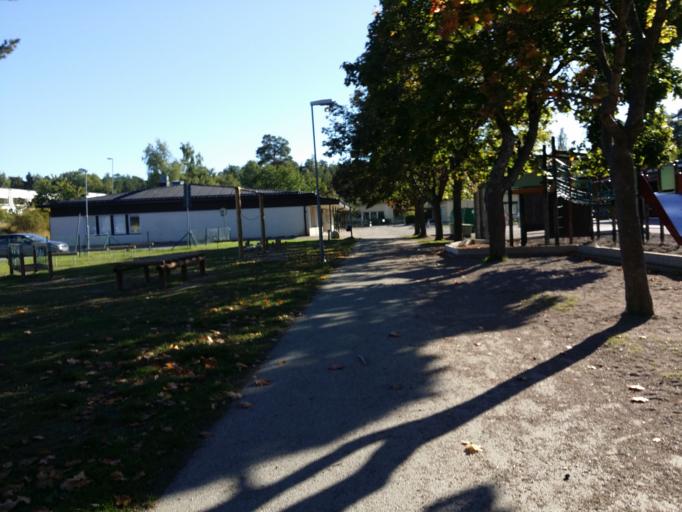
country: SE
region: Stockholm
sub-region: Upplands-Bro Kommun
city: Kungsaengen
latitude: 59.4848
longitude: 17.7214
